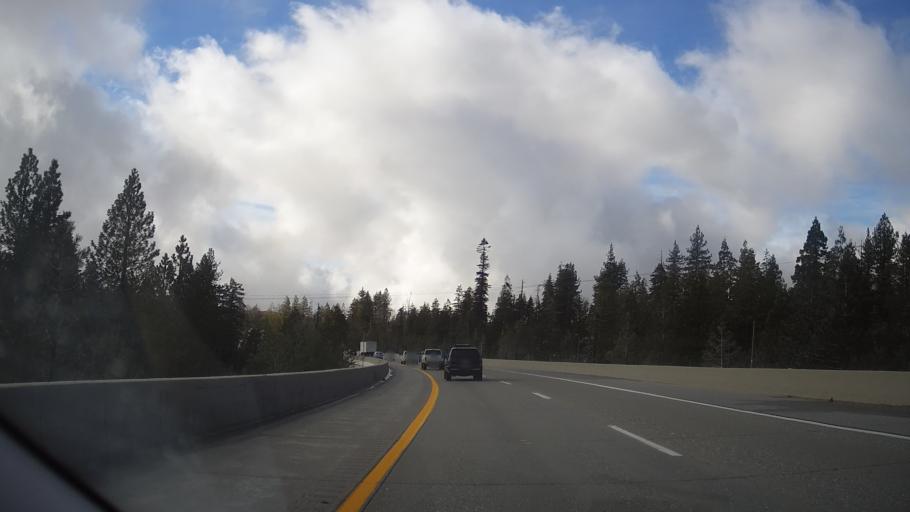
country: US
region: California
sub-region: Sierra County
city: Downieville
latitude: 39.3158
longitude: -120.6213
